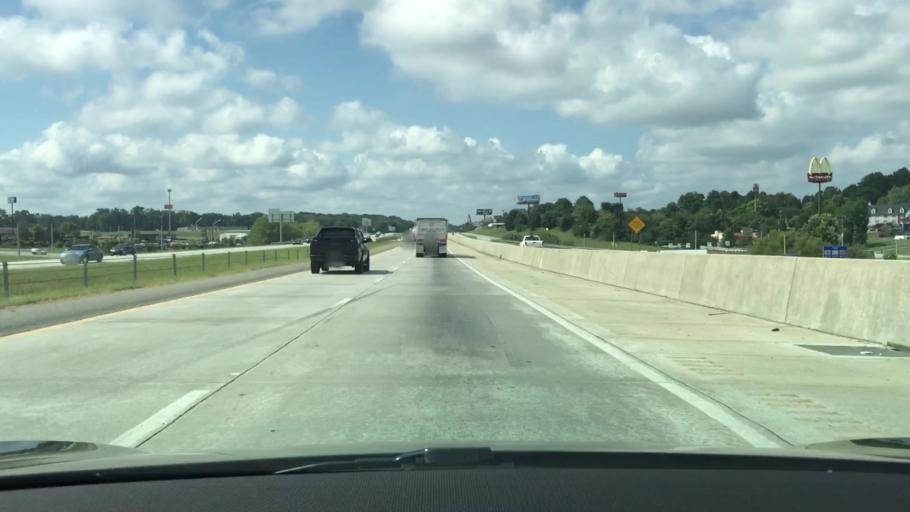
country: US
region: Georgia
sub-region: Hall County
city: Oakwood
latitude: 34.2272
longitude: -83.8634
